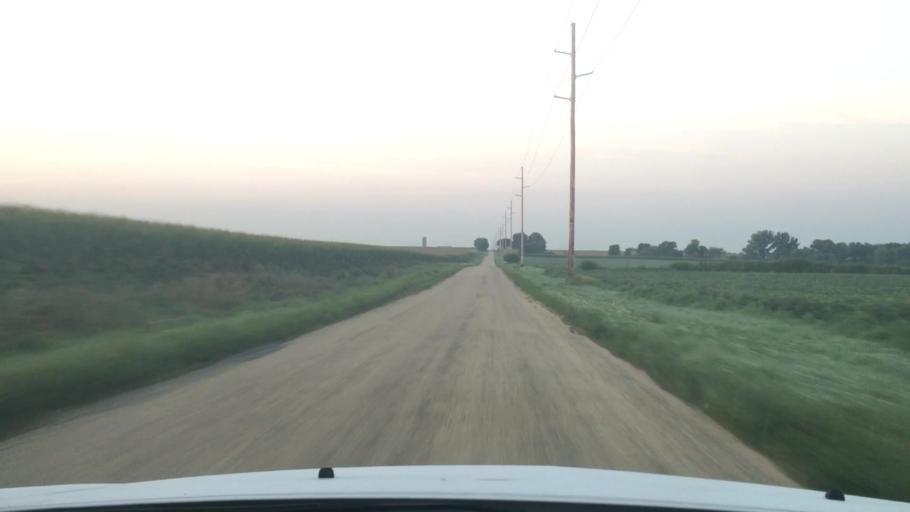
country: US
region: Illinois
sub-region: Ogle County
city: Rochelle
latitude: 41.8707
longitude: -89.0008
